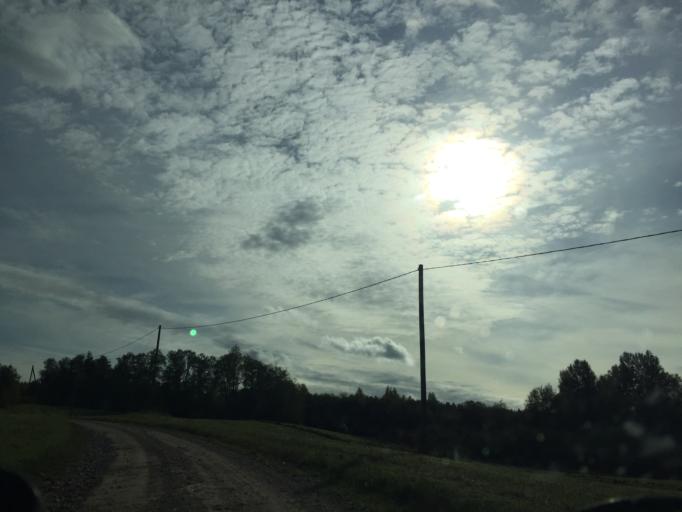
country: LV
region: Jaunpils
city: Jaunpils
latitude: 56.6064
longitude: 22.9976
